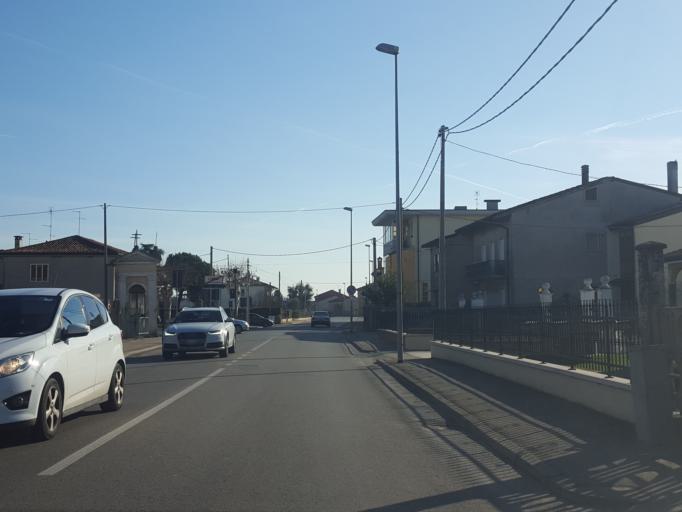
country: IT
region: Veneto
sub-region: Provincia di Verona
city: Locara
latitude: 45.3982
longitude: 11.3338
